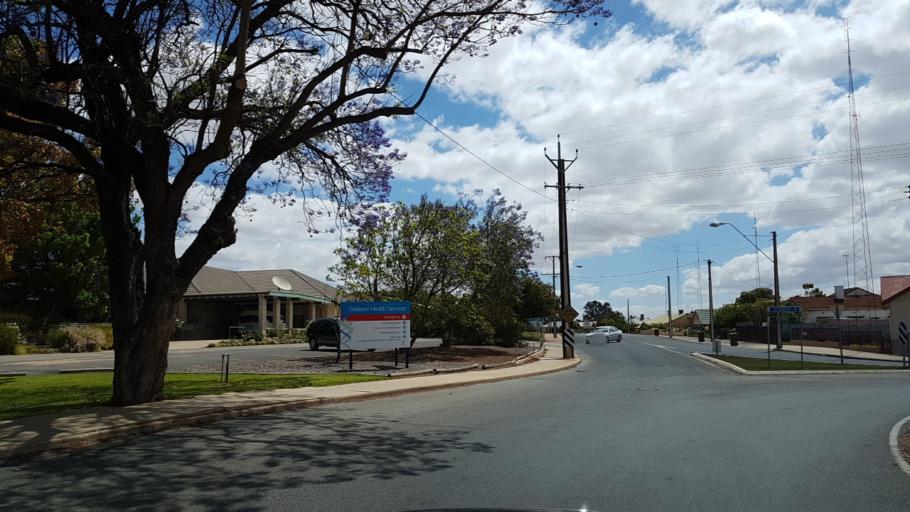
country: AU
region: South Australia
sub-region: Loxton Waikerie
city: Waikerie
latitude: -34.1819
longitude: 139.9857
